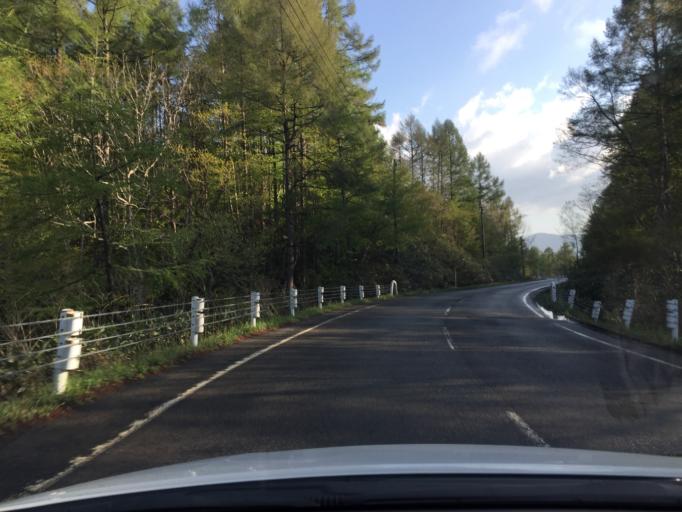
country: JP
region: Fukushima
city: Inawashiro
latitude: 37.6656
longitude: 140.0410
